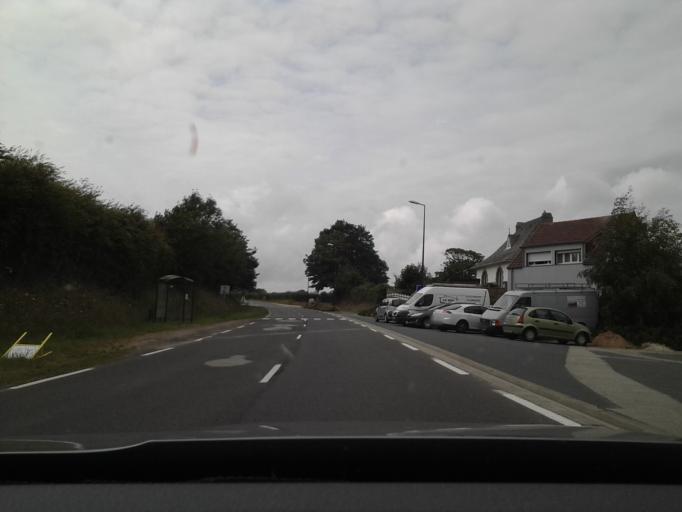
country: FR
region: Lower Normandy
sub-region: Departement de la Manche
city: Urville-Nacqueville
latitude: 49.6682
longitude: -1.7144
